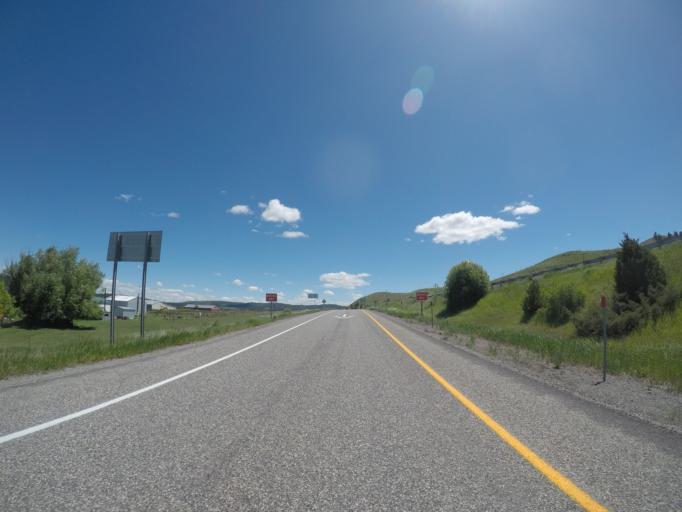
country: US
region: Montana
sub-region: Stillwater County
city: Absarokee
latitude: 45.7056
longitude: -109.5408
